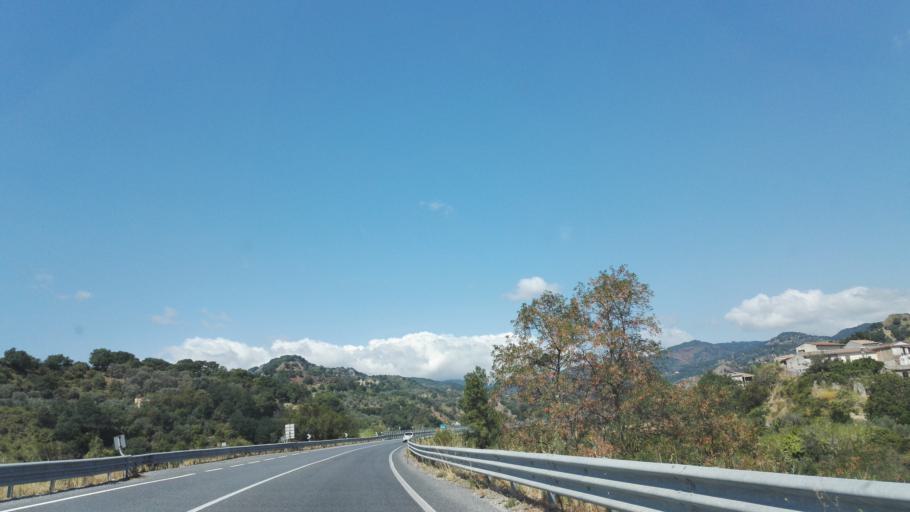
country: IT
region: Calabria
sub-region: Provincia di Reggio Calabria
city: Grotteria
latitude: 38.3438
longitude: 16.2629
